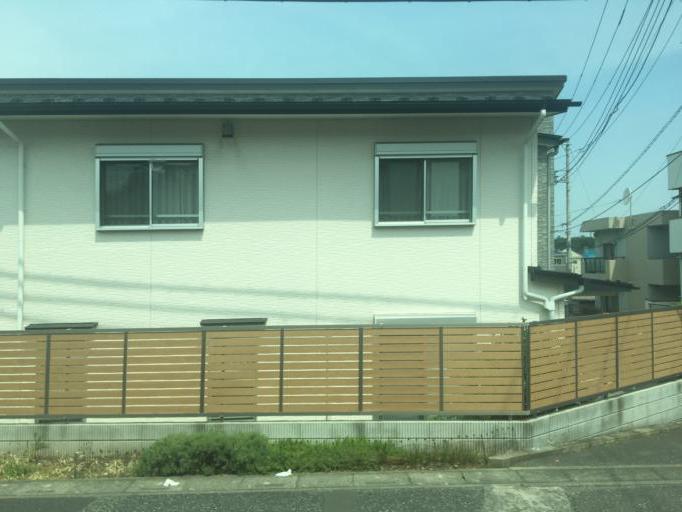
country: JP
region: Tokyo
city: Tanashicho
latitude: 35.7669
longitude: 139.5582
